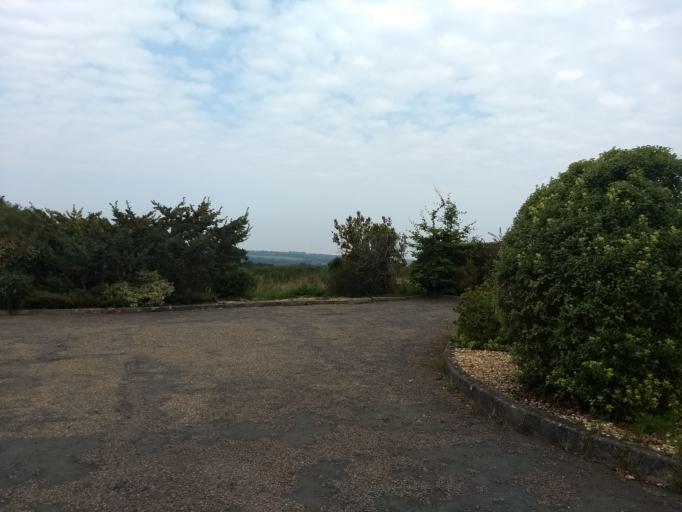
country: GB
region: England
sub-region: Isle of Wight
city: Newport
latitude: 50.7015
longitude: -1.2737
